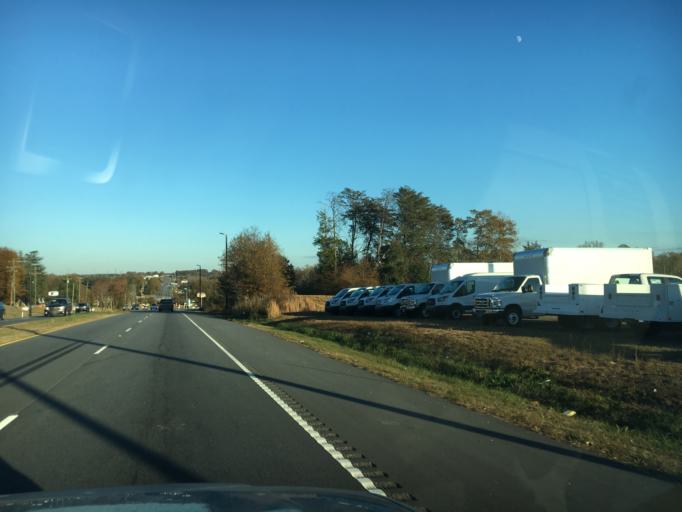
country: US
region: South Carolina
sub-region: Greenville County
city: Greer
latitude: 34.9495
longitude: -82.1948
